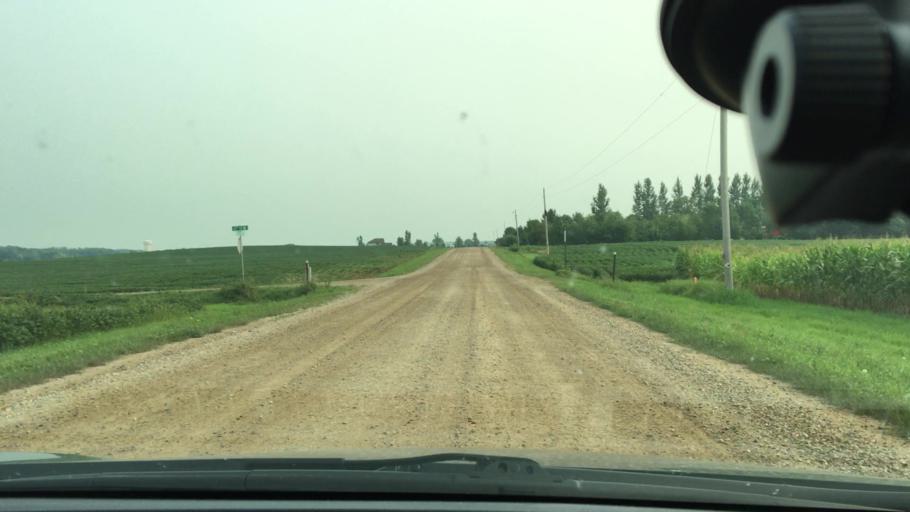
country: US
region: Minnesota
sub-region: Wright County
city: Albertville
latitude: 45.2492
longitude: -93.6274
